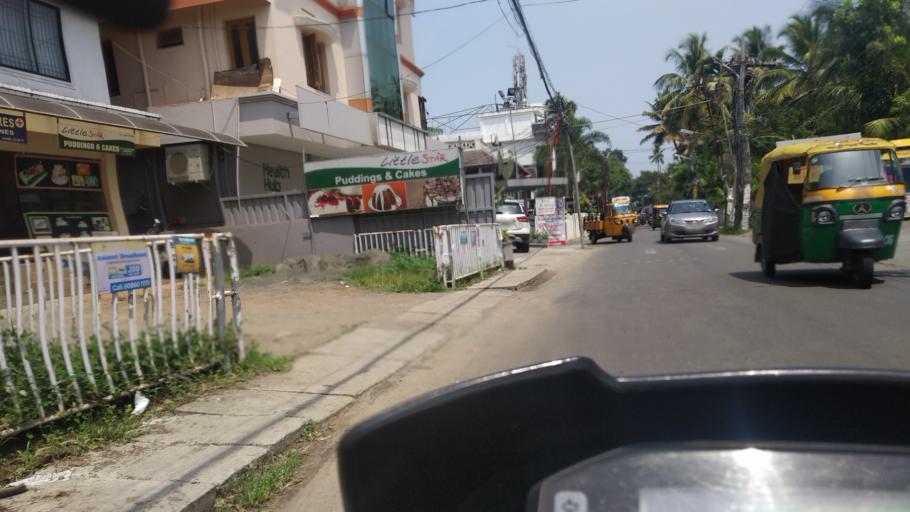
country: IN
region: Kerala
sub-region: Ernakulam
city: Cochin
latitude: 9.9546
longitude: 76.3023
